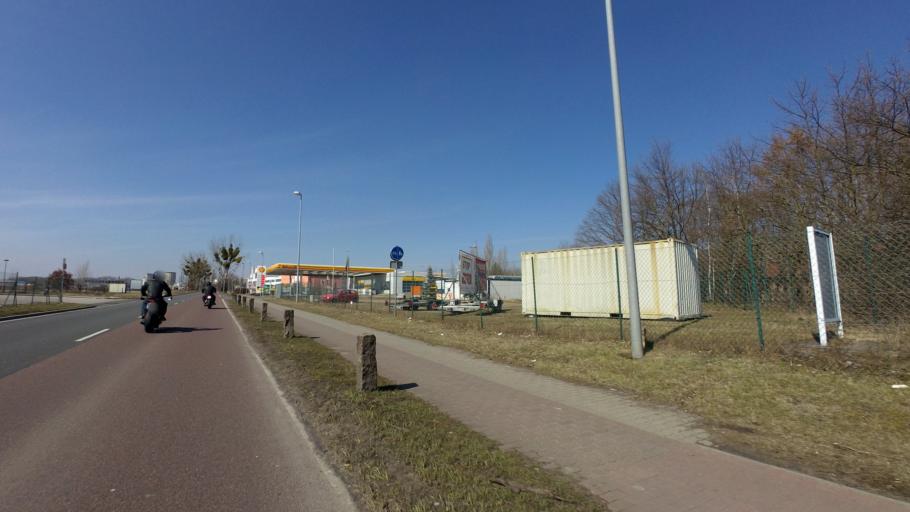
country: DE
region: Saxony-Anhalt
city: Coswig
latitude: 51.8841
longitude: 12.4343
